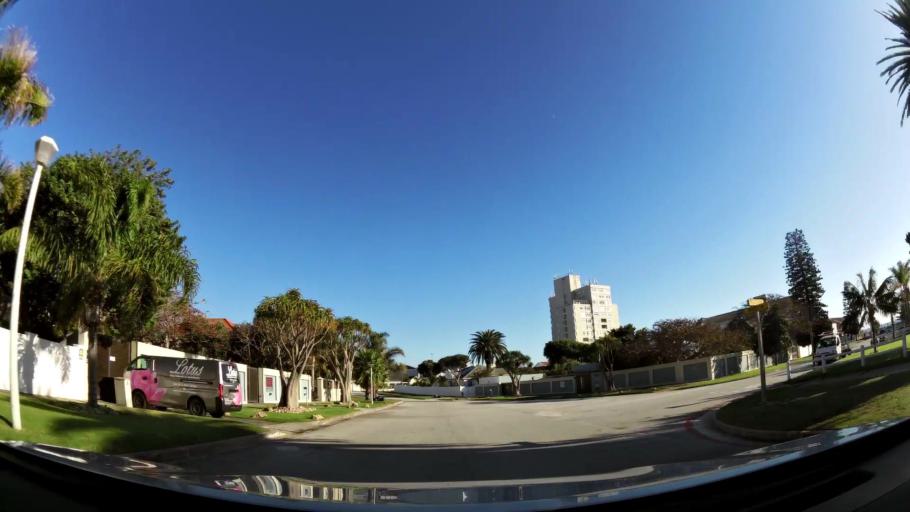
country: ZA
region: Eastern Cape
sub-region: Nelson Mandela Bay Metropolitan Municipality
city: Port Elizabeth
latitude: -33.9845
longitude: 25.6624
